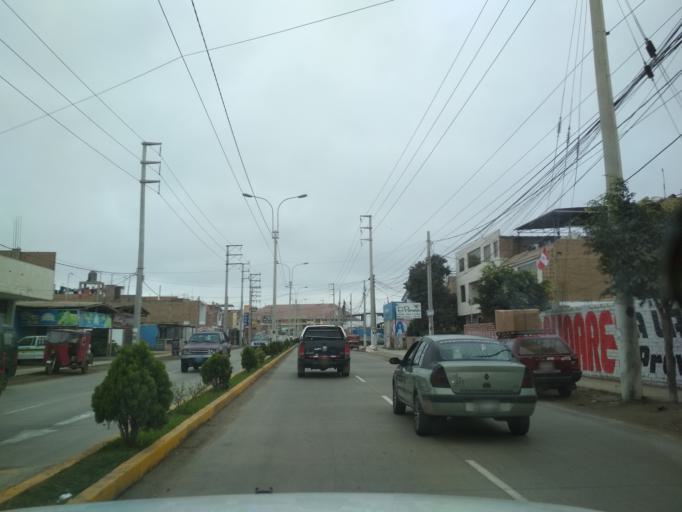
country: PE
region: Lima
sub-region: Provincia de Canete
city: San Vicente de Canete
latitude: -13.0745
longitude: -76.3724
